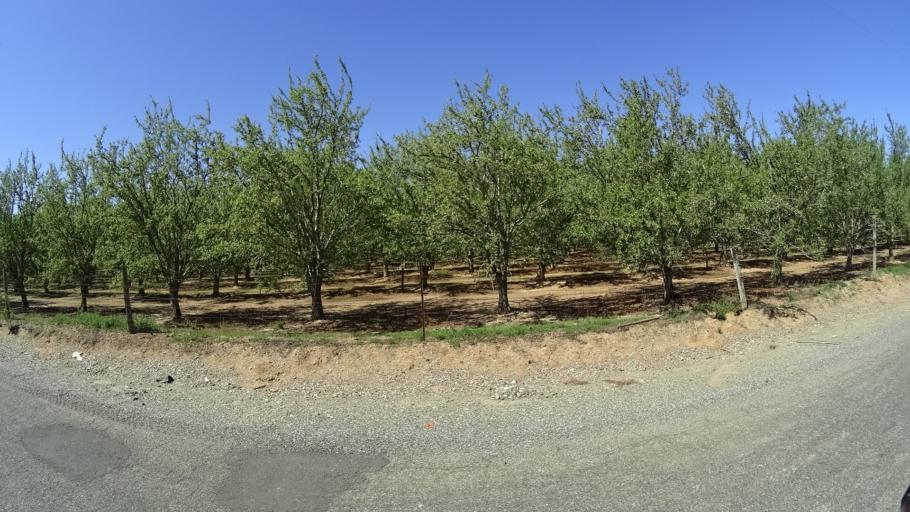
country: US
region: California
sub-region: Glenn County
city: Orland
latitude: 39.6780
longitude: -122.2531
